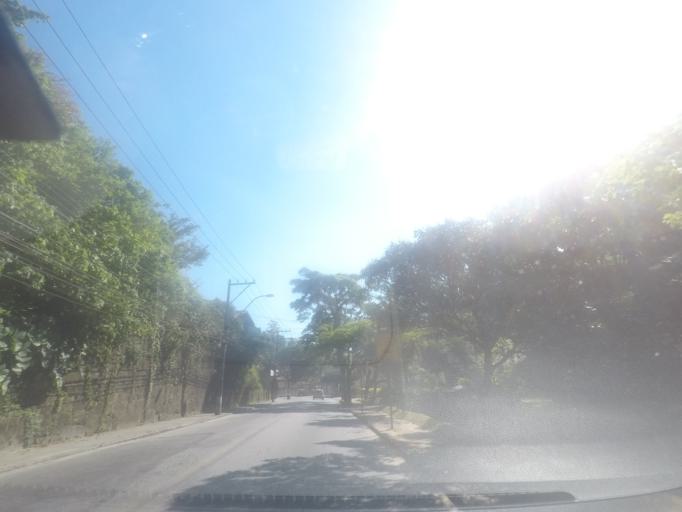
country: BR
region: Rio de Janeiro
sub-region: Petropolis
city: Petropolis
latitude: -22.5316
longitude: -43.1993
